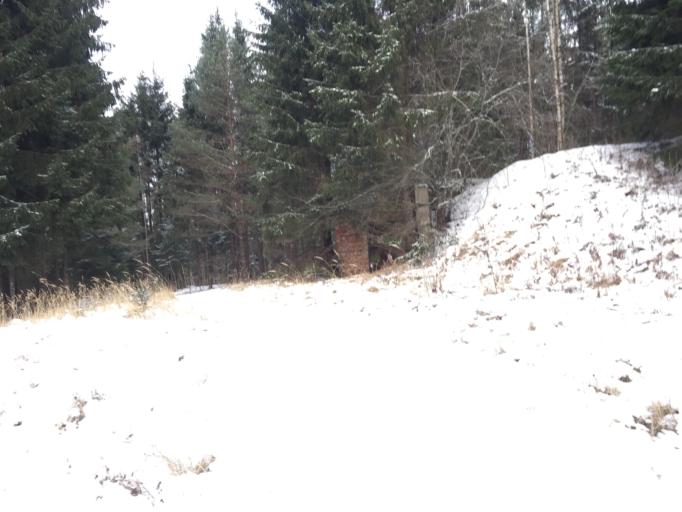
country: LV
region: Amatas Novads
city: Drabesi
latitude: 57.2185
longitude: 25.1664
